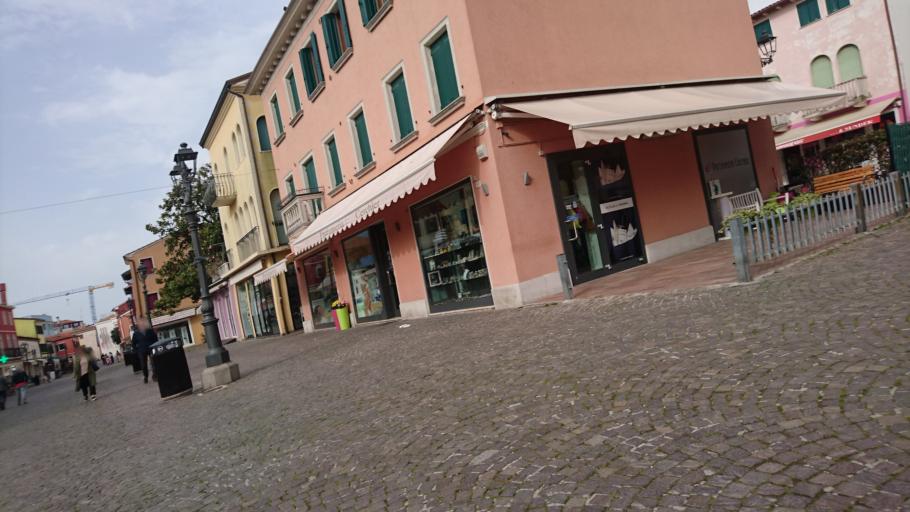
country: IT
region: Veneto
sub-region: Provincia di Venezia
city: Caorle
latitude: 45.5995
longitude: 12.8882
